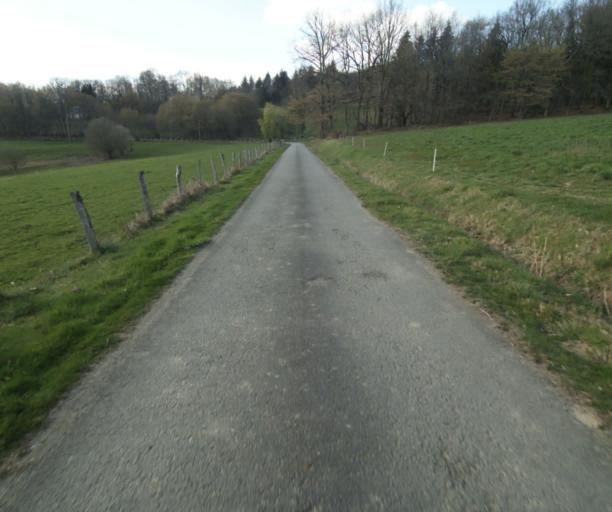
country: FR
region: Limousin
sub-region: Departement de la Correze
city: Saint-Mexant
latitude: 45.3416
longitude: 1.6035
